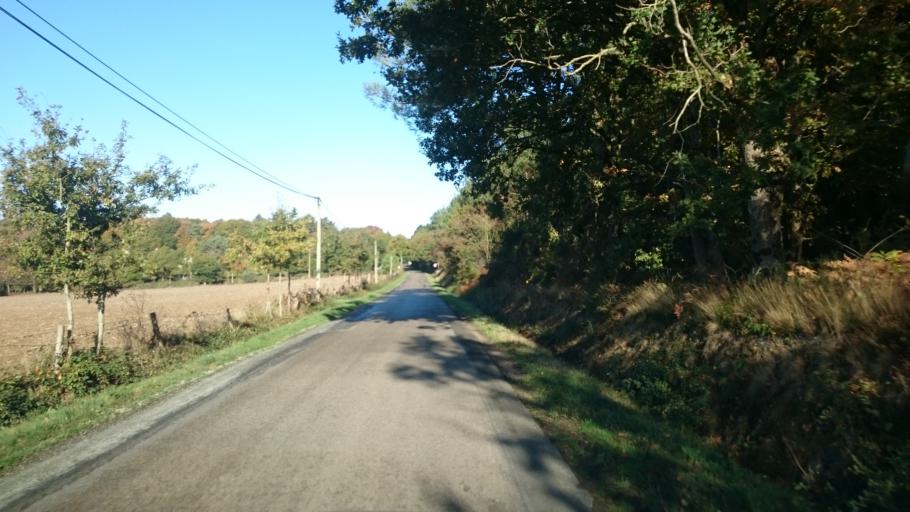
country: FR
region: Brittany
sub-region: Departement d'Ille-et-Vilaine
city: Laille
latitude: 47.9663
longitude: -1.7066
